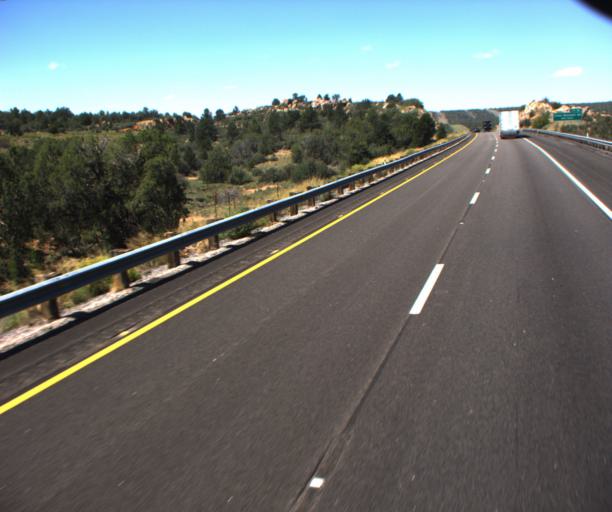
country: US
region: Arizona
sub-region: Mohave County
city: Peach Springs
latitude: 35.2090
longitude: -113.2892
